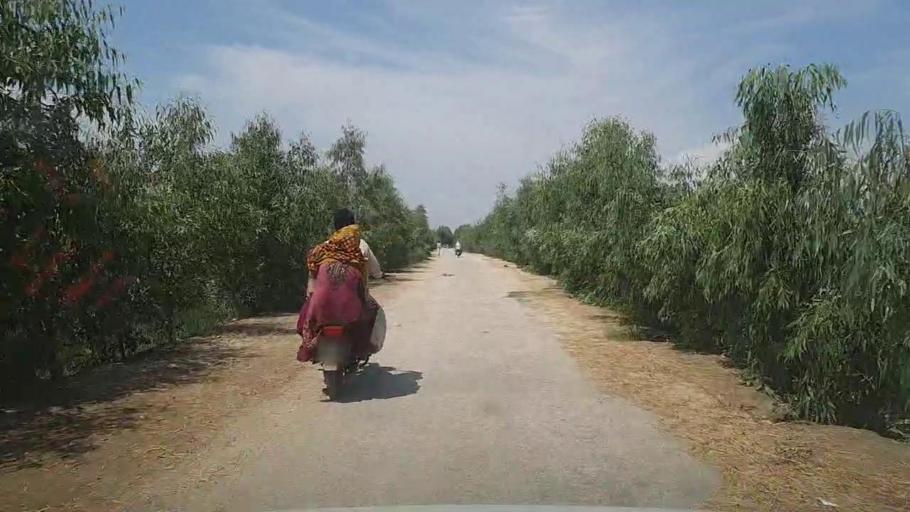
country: PK
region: Sindh
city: Kandhkot
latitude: 28.2932
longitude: 69.2377
